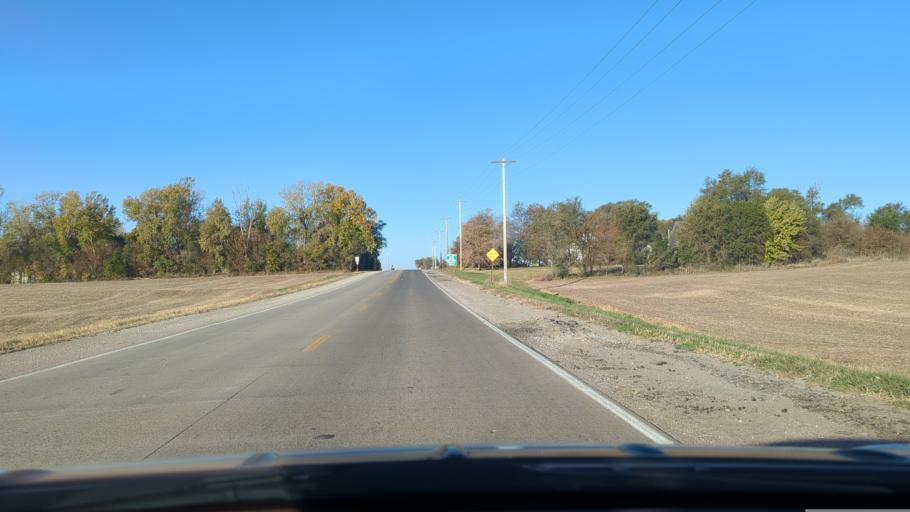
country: US
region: Nebraska
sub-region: Sarpy County
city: Springfield
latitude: 41.1036
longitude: -96.1547
